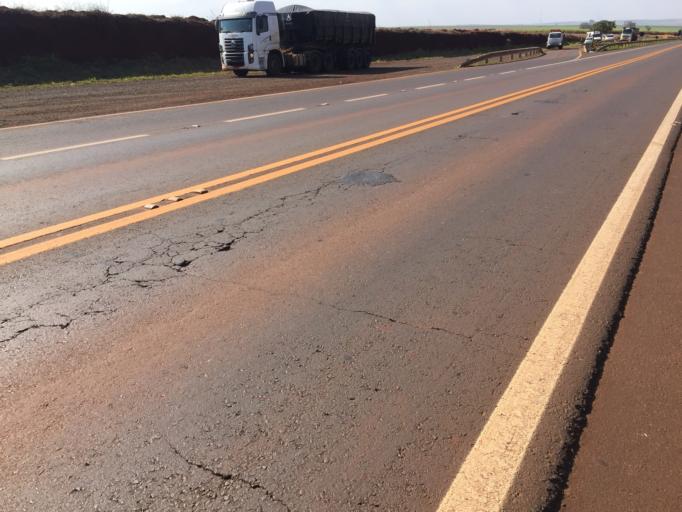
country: BR
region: Sao Paulo
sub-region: Pradopolis
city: Pradopolis
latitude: -21.3324
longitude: -48.0535
